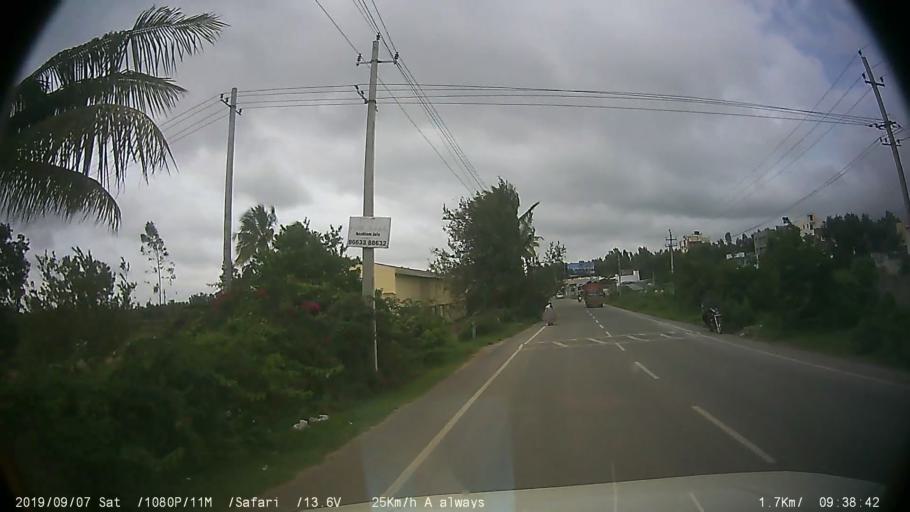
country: IN
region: Karnataka
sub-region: Bangalore Urban
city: Anekal
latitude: 12.8170
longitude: 77.6281
